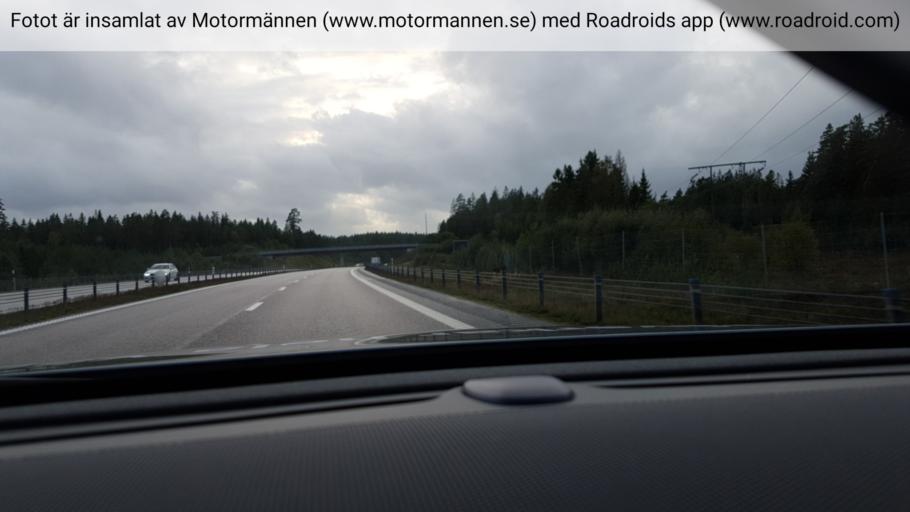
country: SE
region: Vaestra Goetaland
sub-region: Uddevalla Kommun
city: Uddevalla
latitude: 58.3305
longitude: 12.0927
